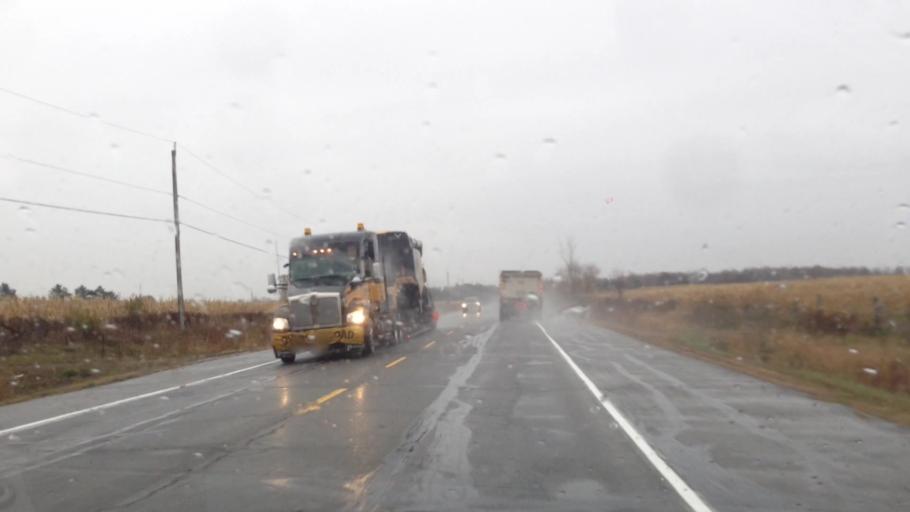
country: CA
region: Ontario
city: Clarence-Rockland
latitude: 45.3504
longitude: -75.3683
